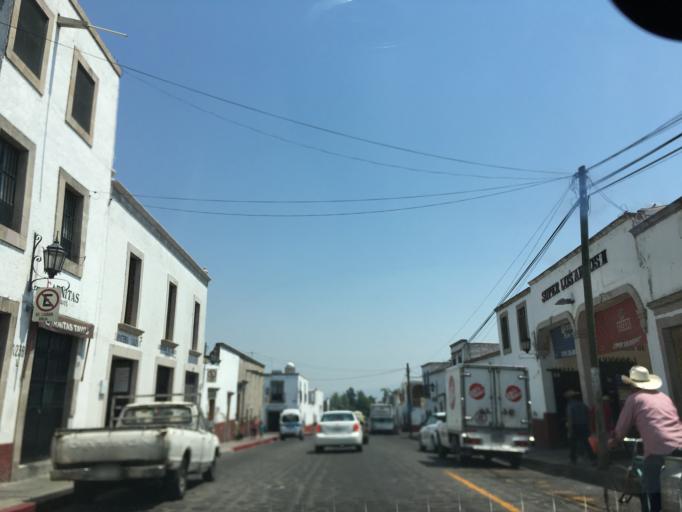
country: MX
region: Michoacan
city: Cuitzeo del Porvenir
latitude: 19.9705
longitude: -101.1395
